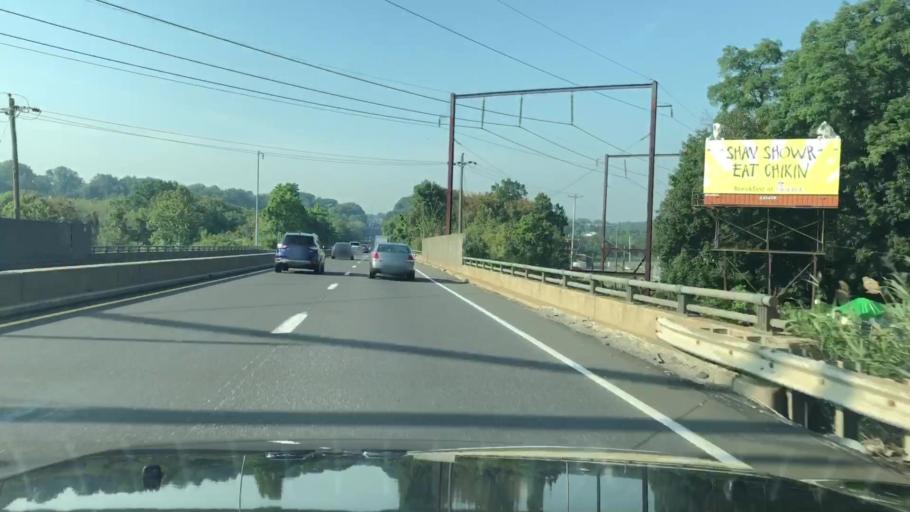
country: US
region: Pennsylvania
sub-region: Bucks County
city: Penndel
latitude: 40.1509
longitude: -74.9495
